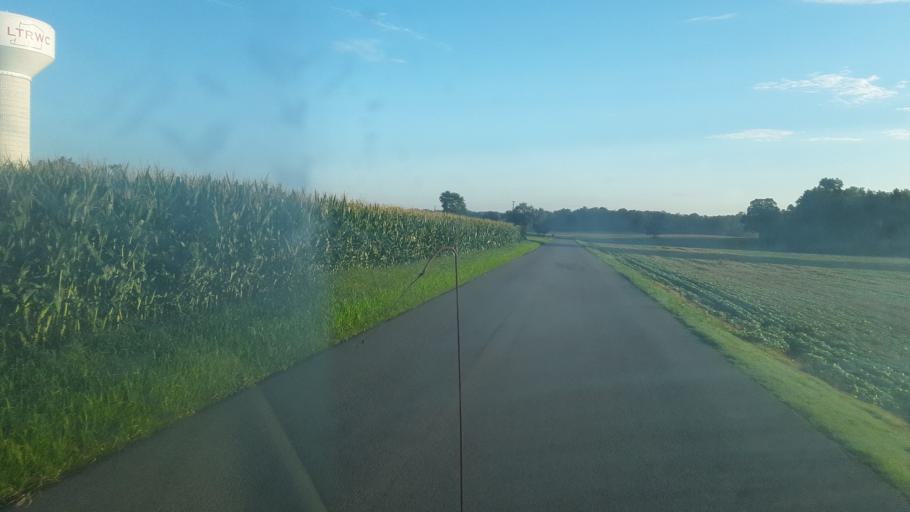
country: US
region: Kentucky
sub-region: Todd County
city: Guthrie
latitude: 36.7045
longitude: -87.1701
